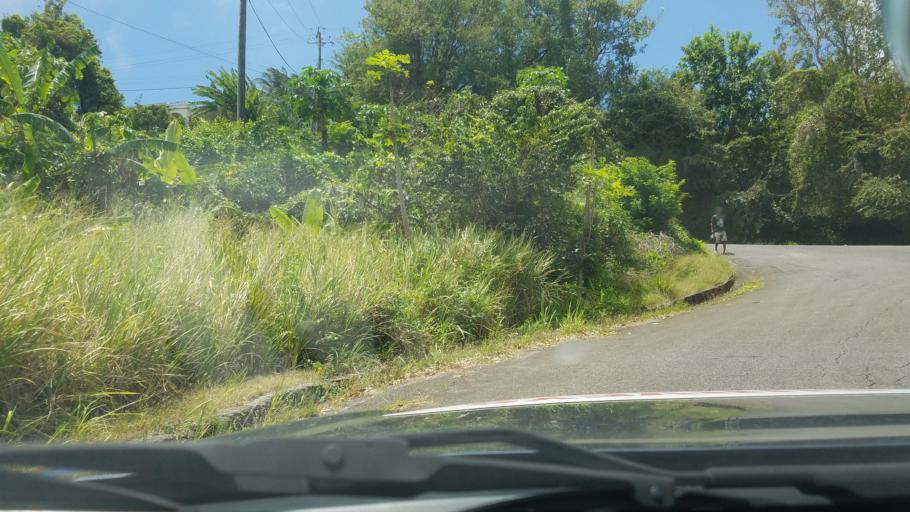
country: LC
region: Gros-Islet
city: Gros Islet
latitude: 14.0559
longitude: -60.9354
